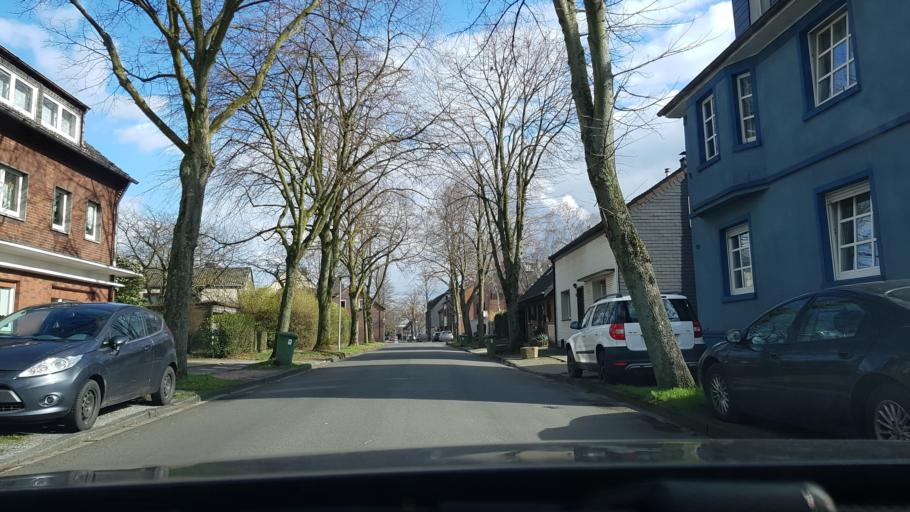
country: DE
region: North Rhine-Westphalia
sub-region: Regierungsbezirk Dusseldorf
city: Oberhausen
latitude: 51.4903
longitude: 6.8235
